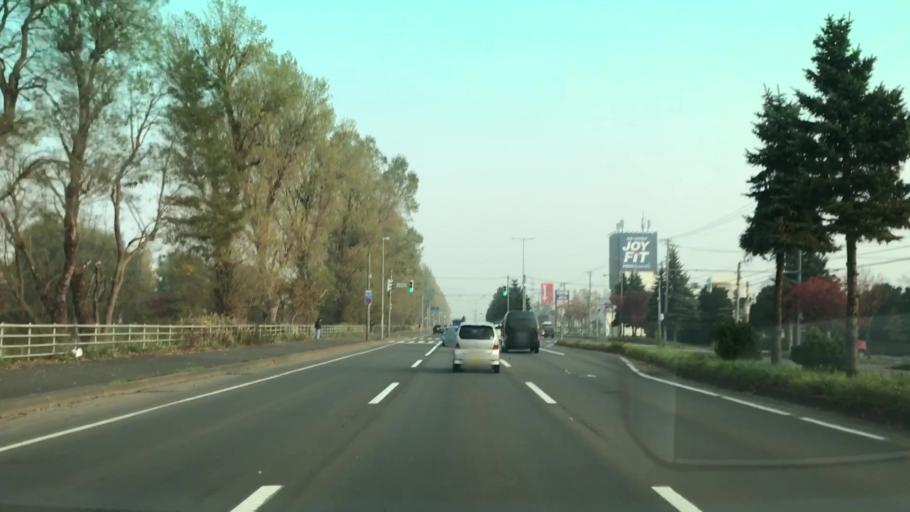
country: JP
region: Hokkaido
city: Sapporo
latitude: 43.1374
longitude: 141.3479
